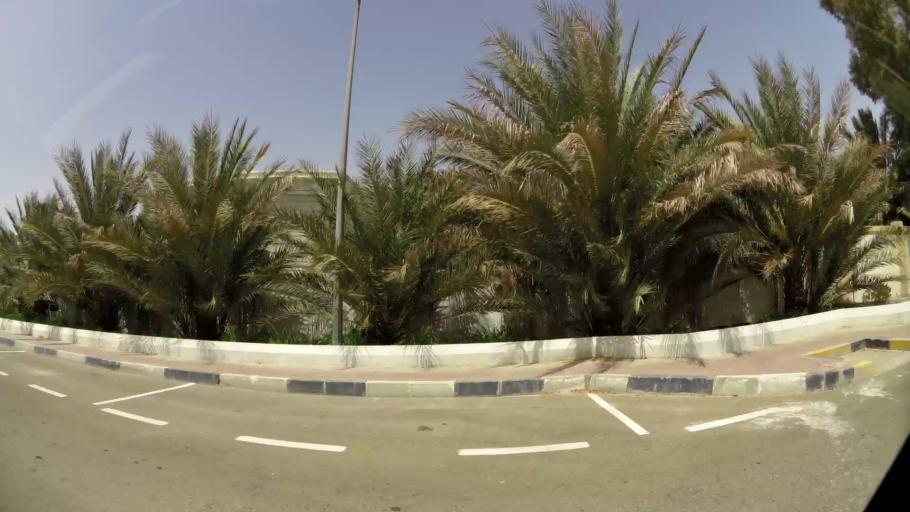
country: AE
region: Abu Dhabi
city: Al Ain
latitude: 24.1771
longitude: 55.7105
